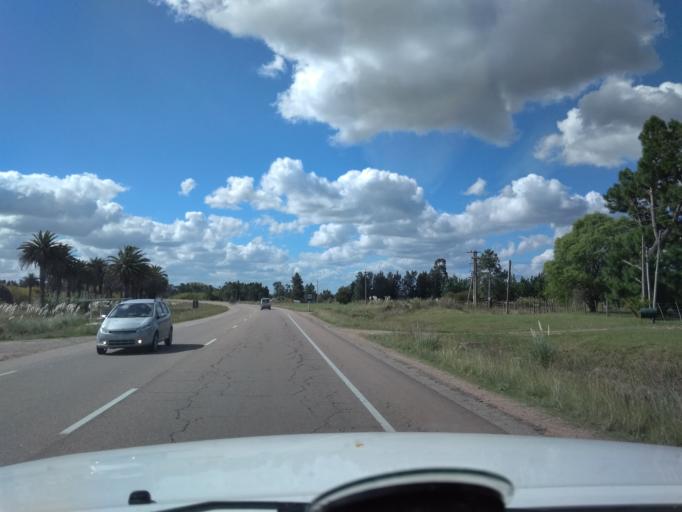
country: UY
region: Canelones
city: Sauce
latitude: -34.6778
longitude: -56.0515
